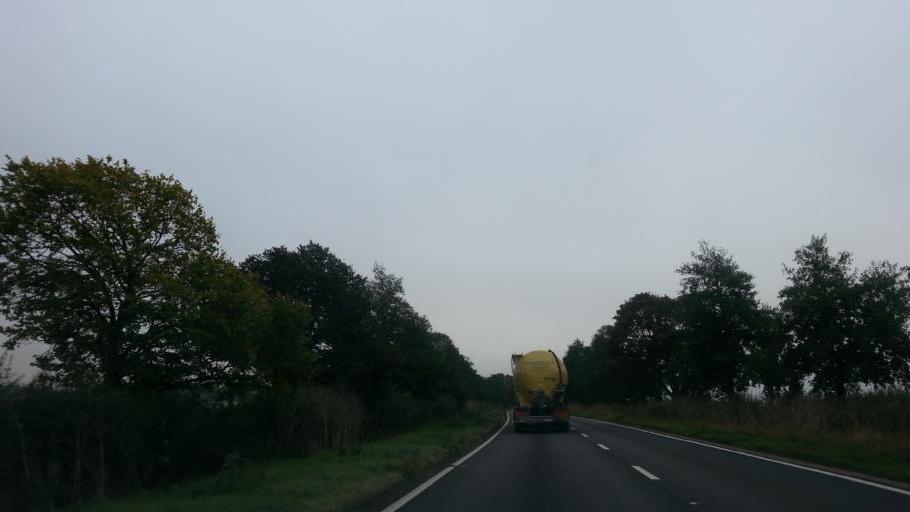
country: GB
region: England
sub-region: Northamptonshire
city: Thrapston
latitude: 52.4182
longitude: -0.4995
